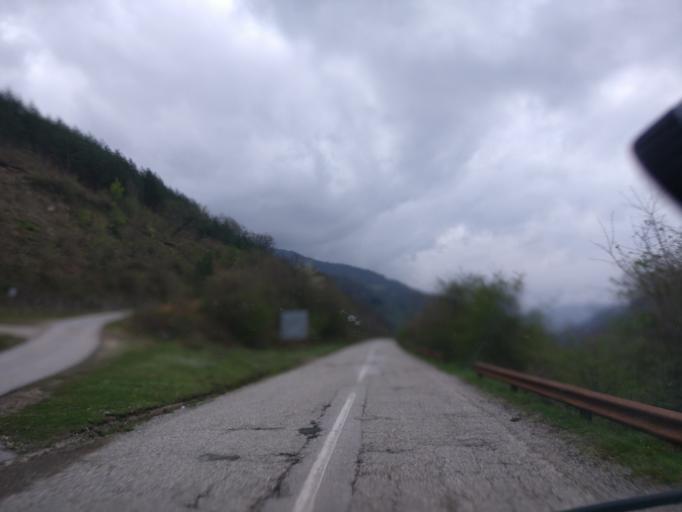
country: BA
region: Republika Srpska
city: Foca
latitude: 43.4449
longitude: 18.7571
